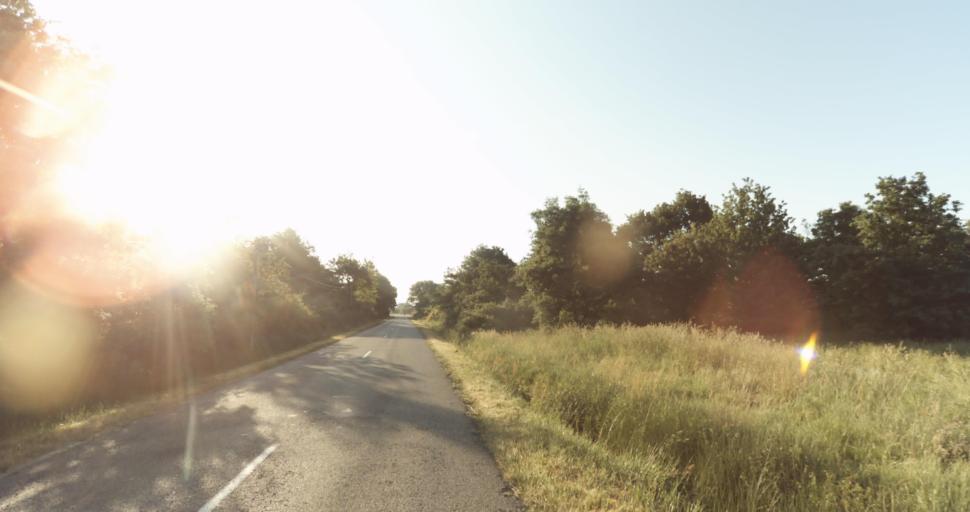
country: FR
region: Midi-Pyrenees
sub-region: Departement de la Haute-Garonne
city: Fontenilles
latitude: 43.5458
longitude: 1.2066
